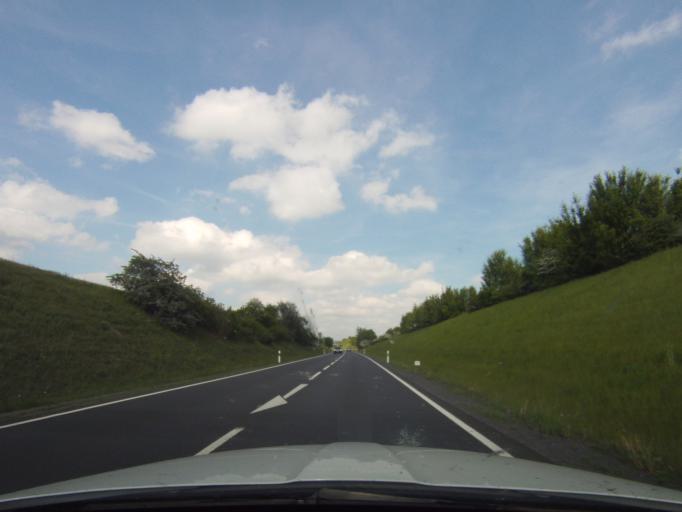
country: DE
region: Thuringia
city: Kospoda
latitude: 50.7292
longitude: 11.7637
